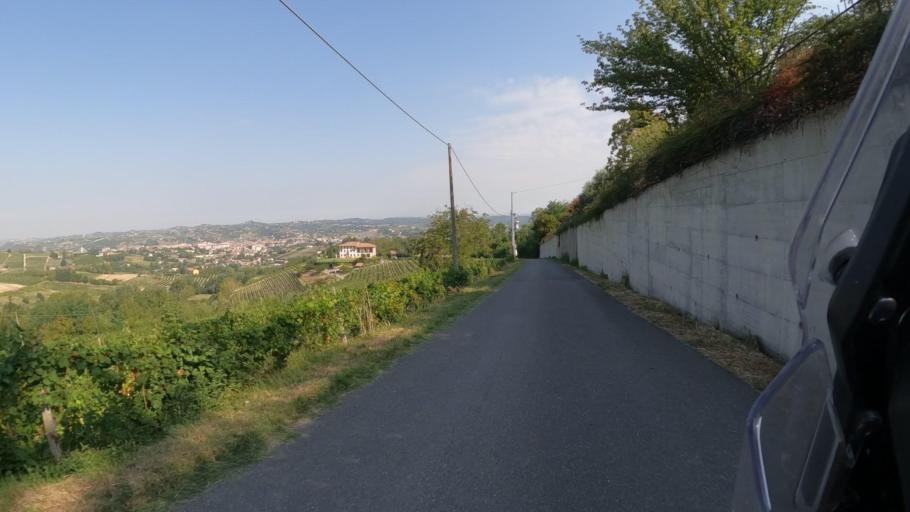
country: IT
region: Piedmont
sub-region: Provincia di Asti
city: Nizza Monferrato
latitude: 44.7559
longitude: 8.3826
